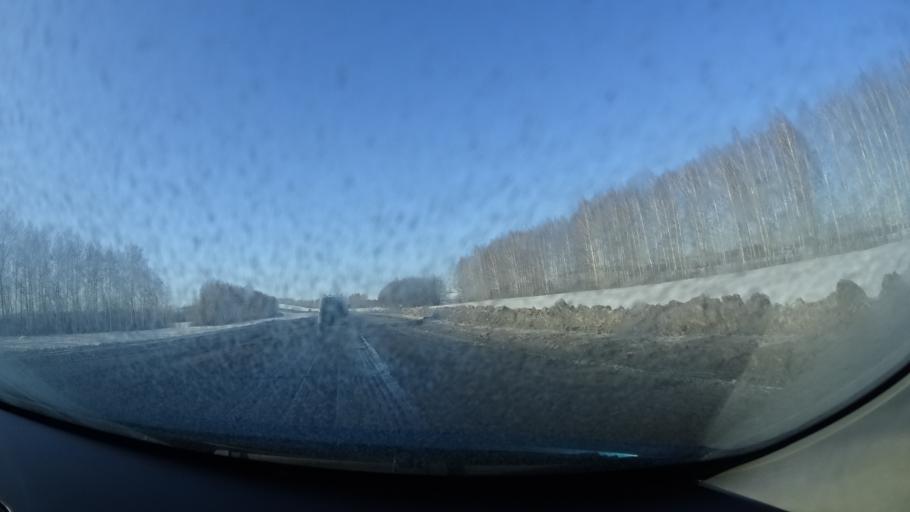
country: RU
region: Bashkortostan
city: Birsk
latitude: 55.2733
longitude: 55.7230
